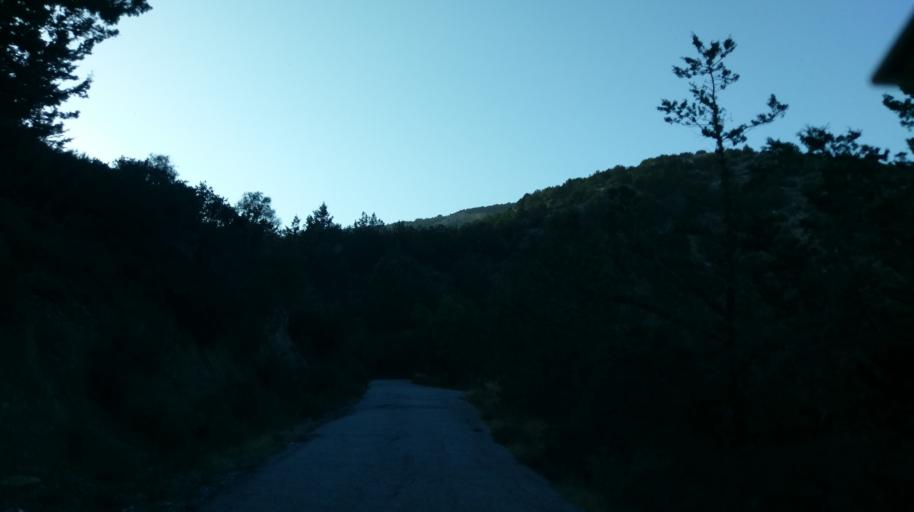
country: CY
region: Ammochostos
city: Trikomo
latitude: 35.3782
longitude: 33.9016
